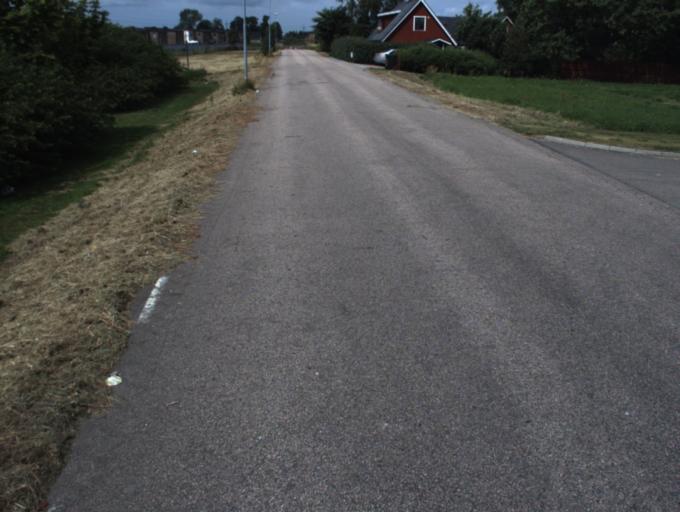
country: SE
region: Skane
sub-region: Helsingborg
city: Rydeback
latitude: 55.9663
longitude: 12.7845
